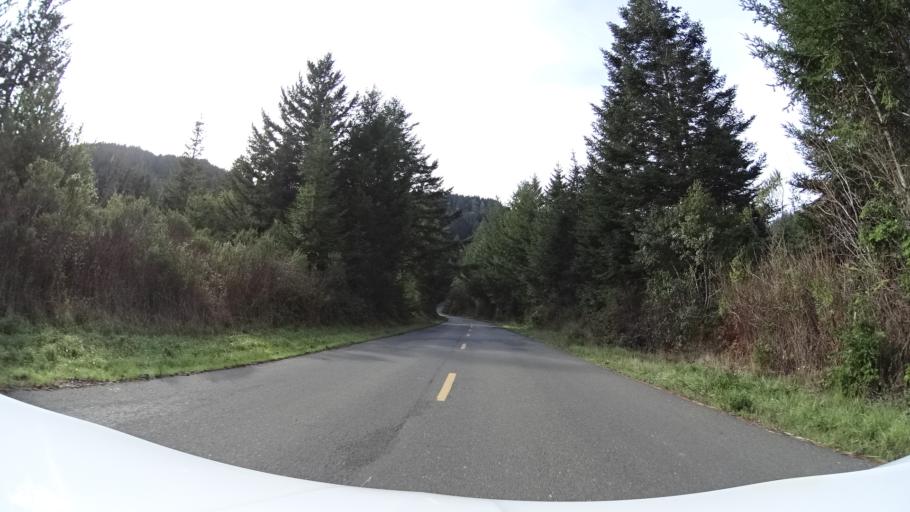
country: US
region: California
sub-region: Humboldt County
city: Ferndale
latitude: 40.3466
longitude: -124.3382
